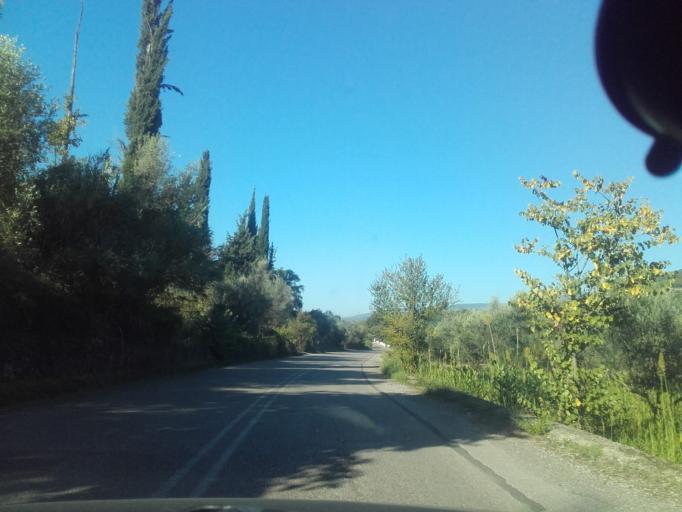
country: GR
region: West Greece
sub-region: Nomos Aitolias kai Akarnanias
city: Nafpaktos
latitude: 38.4171
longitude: 21.9132
